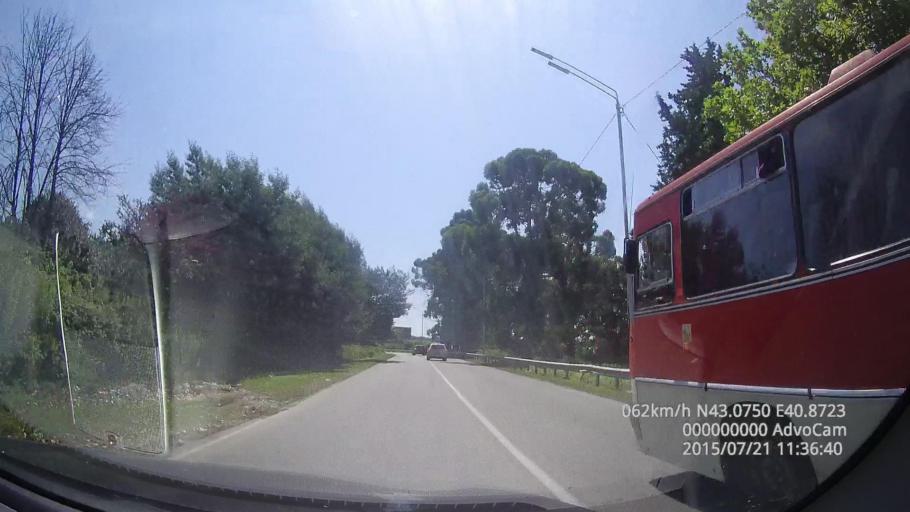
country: GE
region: Abkhazia
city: Stantsiya Novyy Afon
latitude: 43.0748
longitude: 40.8728
